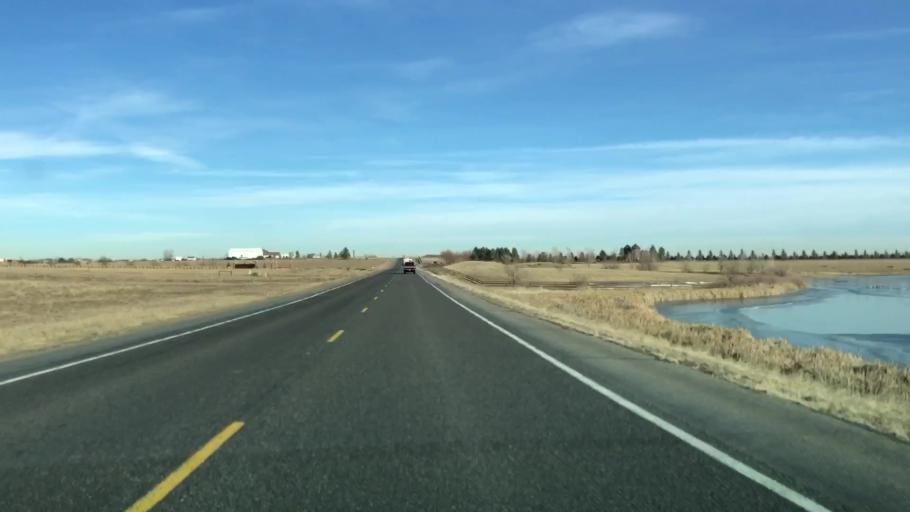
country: US
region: Colorado
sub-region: Weld County
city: Windsor
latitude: 40.4247
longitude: -104.9447
